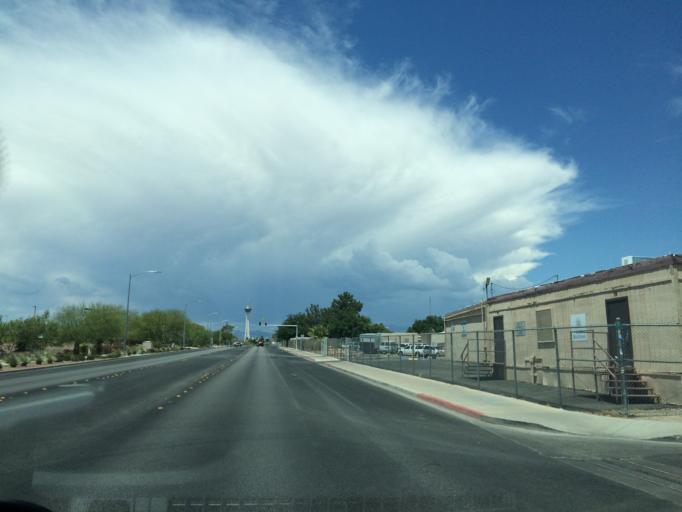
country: US
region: Nevada
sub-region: Clark County
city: Winchester
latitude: 36.1481
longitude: -115.1111
